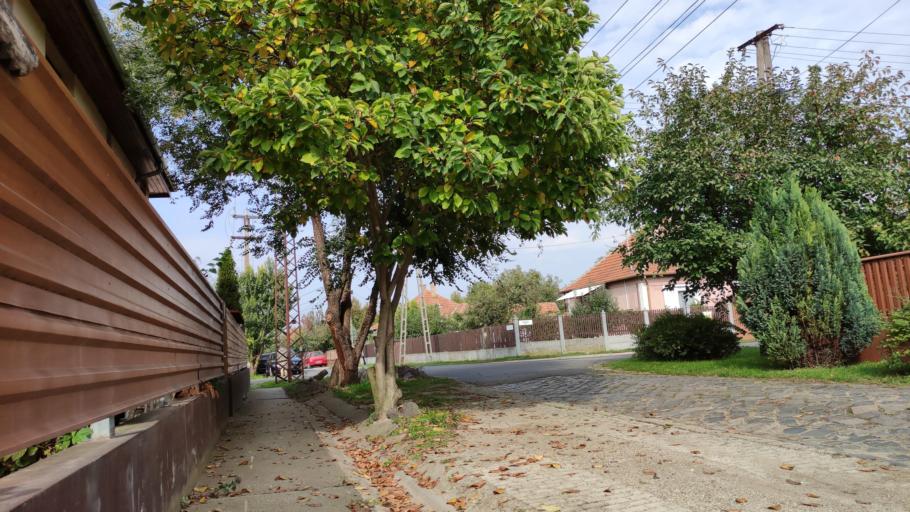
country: HU
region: Hajdu-Bihar
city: Hajduboszormeny
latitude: 47.6839
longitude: 21.5050
